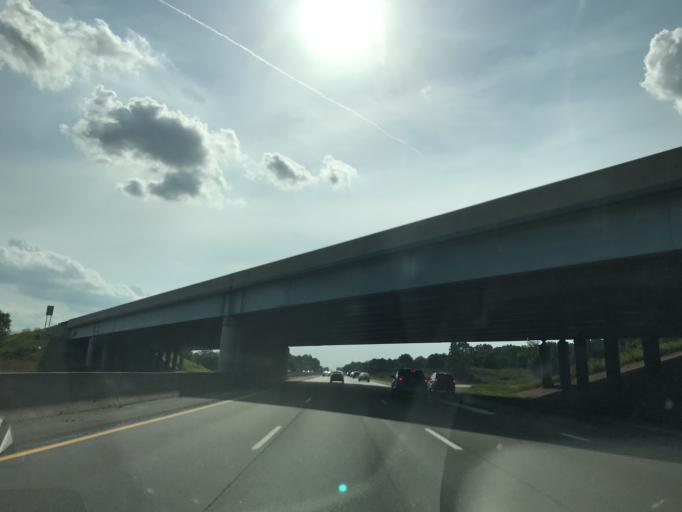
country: US
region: Michigan
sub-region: Washtenaw County
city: Ypsilanti
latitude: 42.2244
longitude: -83.6506
